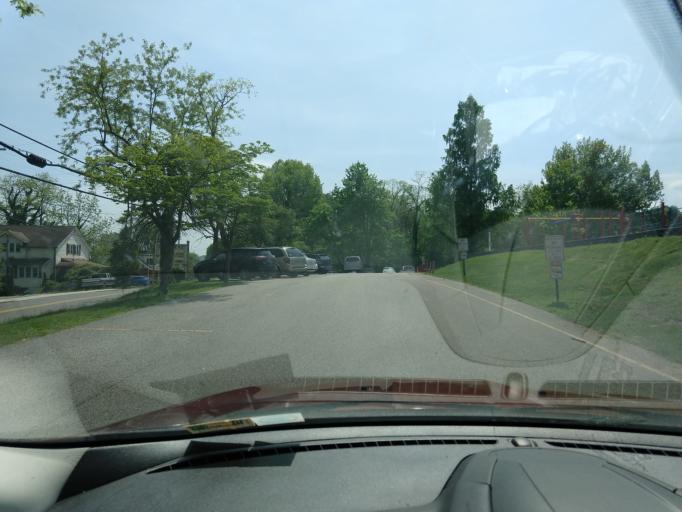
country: US
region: West Virginia
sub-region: Kanawha County
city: Saint Albans
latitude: 38.3834
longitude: -81.8313
